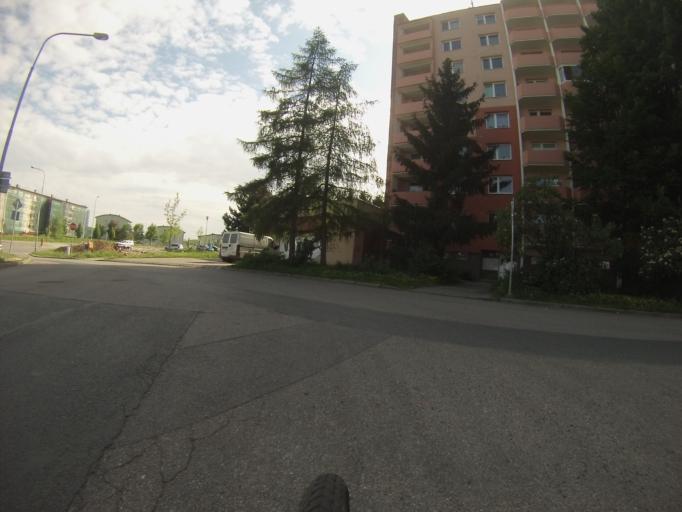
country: CZ
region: South Moravian
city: Troubsko
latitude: 49.2189
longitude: 16.5191
